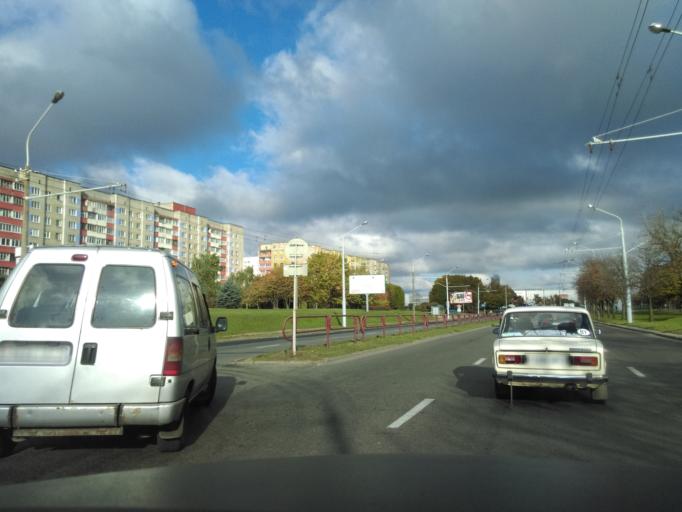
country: BY
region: Minsk
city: Minsk
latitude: 53.8714
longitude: 27.5988
